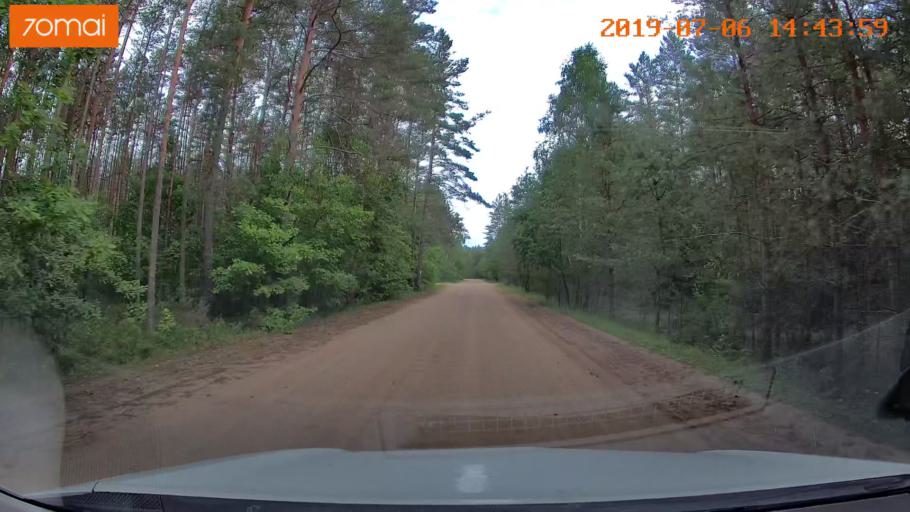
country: BY
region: Minsk
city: Ivyanyets
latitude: 53.9570
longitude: 26.6946
